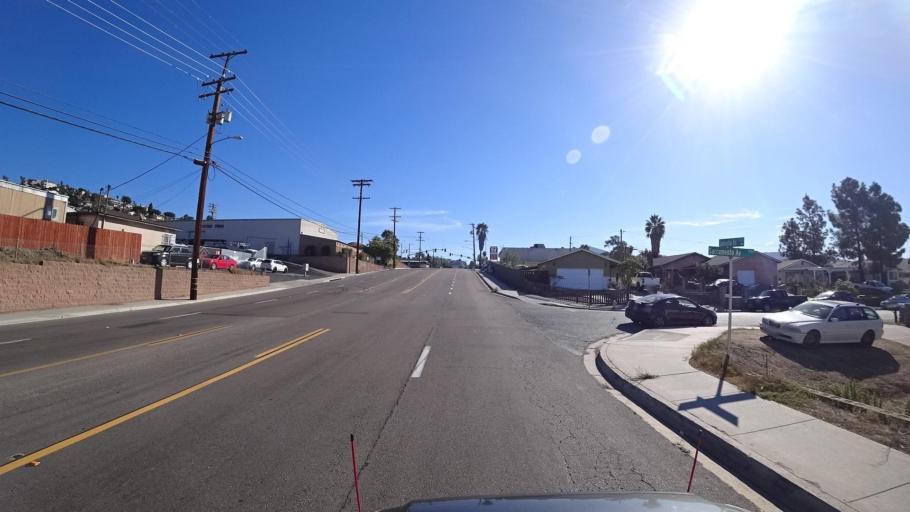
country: US
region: California
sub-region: San Diego County
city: La Presa
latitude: 32.7148
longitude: -116.9988
